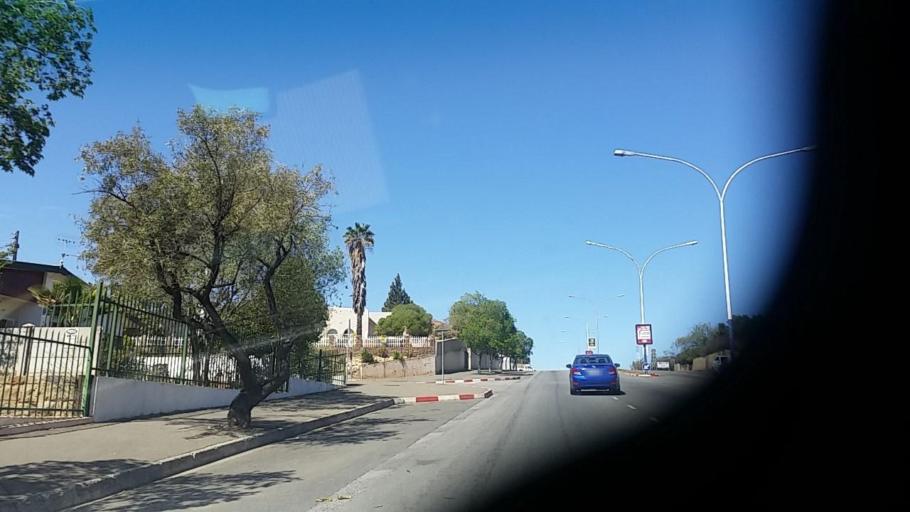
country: ZA
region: Western Cape
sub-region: Eden District Municipality
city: Oudtshoorn
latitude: -33.5938
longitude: 22.2103
